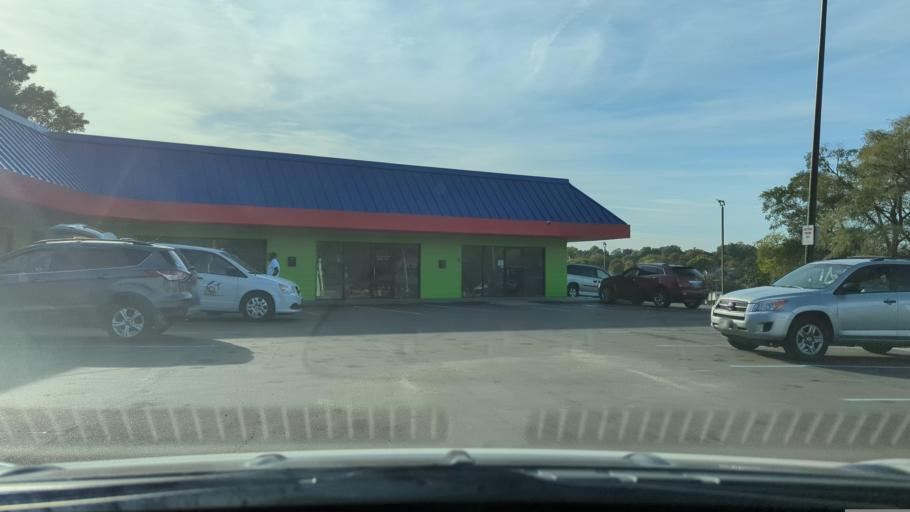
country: US
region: Nebraska
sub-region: Sarpy County
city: Bellevue
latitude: 41.1623
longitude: -95.9225
